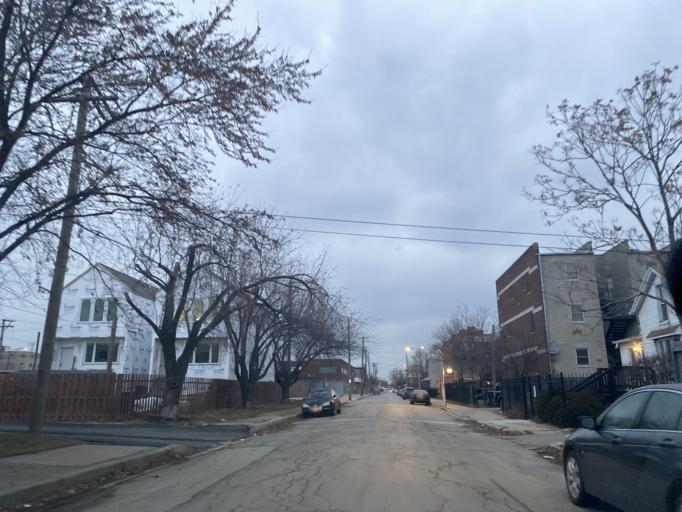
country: US
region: Illinois
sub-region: Cook County
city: Chicago
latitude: 41.8678
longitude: -87.6885
